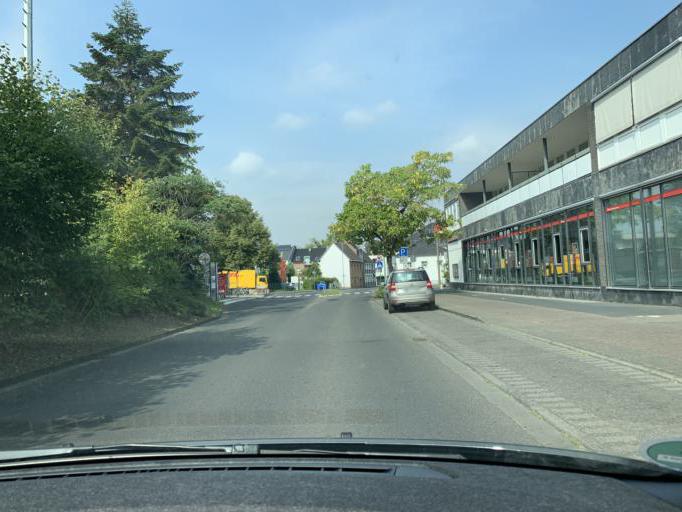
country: DE
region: North Rhine-Westphalia
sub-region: Regierungsbezirk Koln
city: Erftstadt
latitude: 50.8131
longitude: 6.8159
